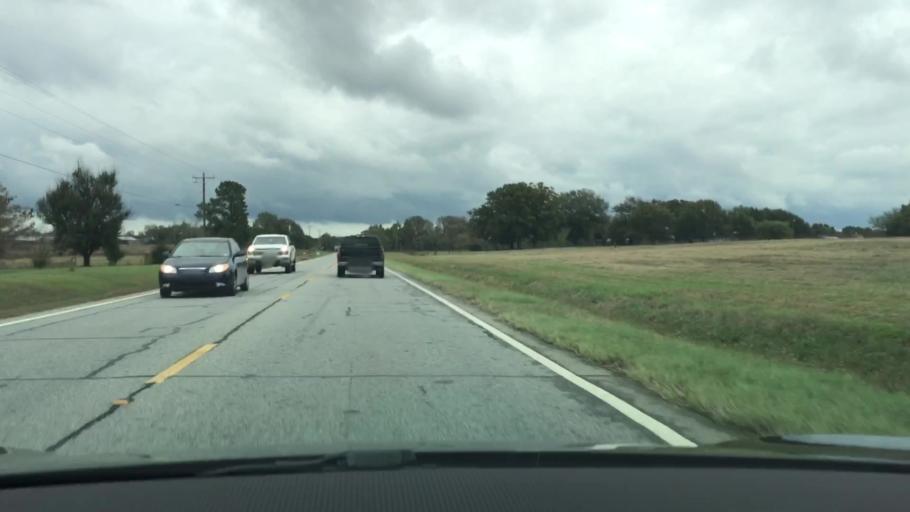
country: US
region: Georgia
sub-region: Oconee County
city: Watkinsville
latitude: 33.8274
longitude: -83.3737
